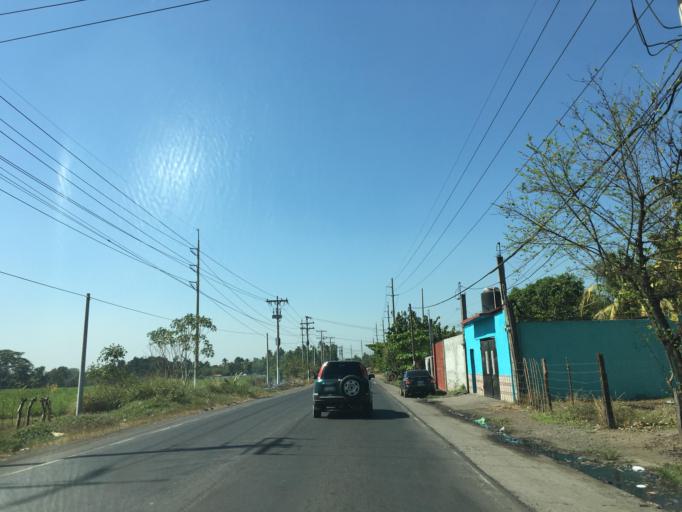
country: GT
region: Escuintla
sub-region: Municipio de Masagua
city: Masagua
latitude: 14.2108
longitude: -90.8388
